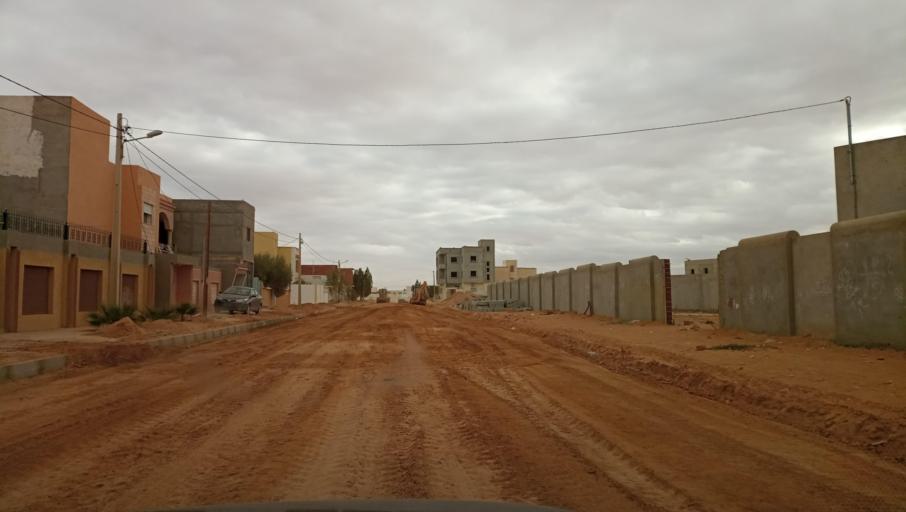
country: TN
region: Tataouine
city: Tataouine
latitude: 32.9875
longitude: 10.4573
